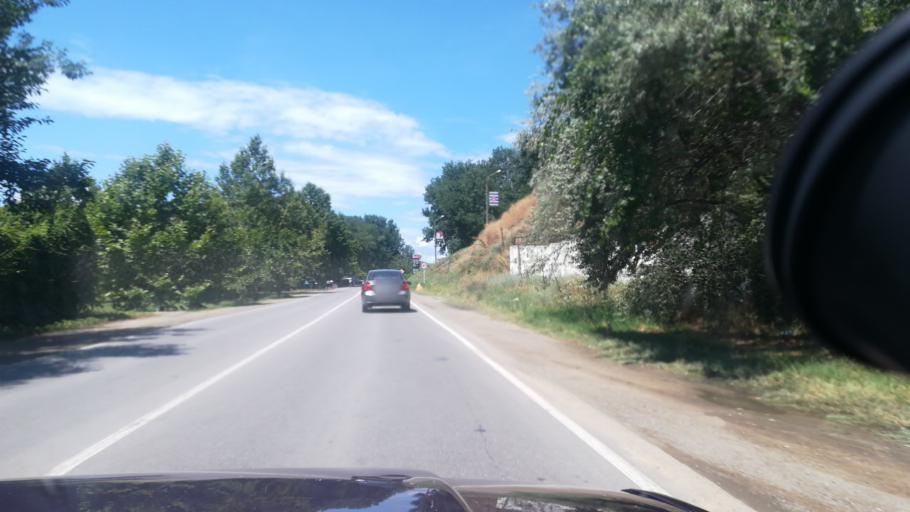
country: RU
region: Krasnodarskiy
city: Vityazevo
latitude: 44.9756
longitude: 37.2754
